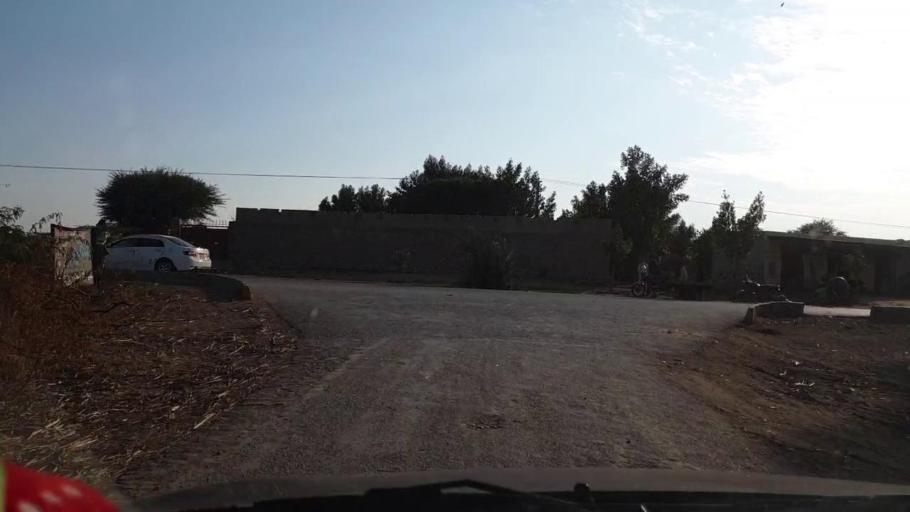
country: PK
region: Sindh
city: Jhol
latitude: 25.9497
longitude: 68.8614
